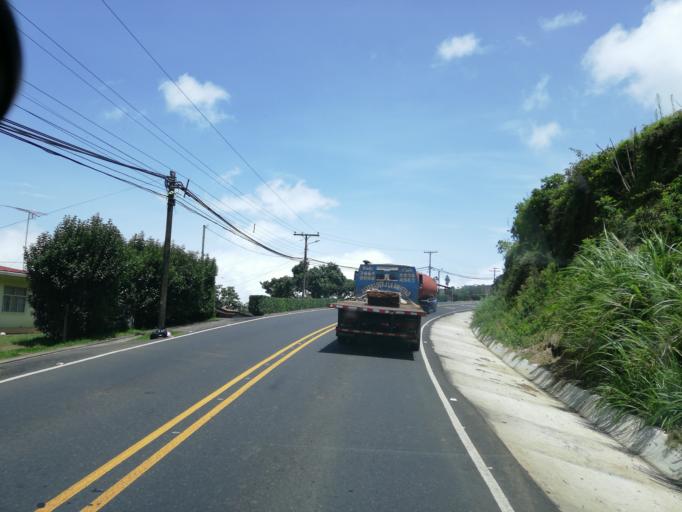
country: CR
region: Alajuela
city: Zarcero
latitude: 10.2157
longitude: -84.3990
